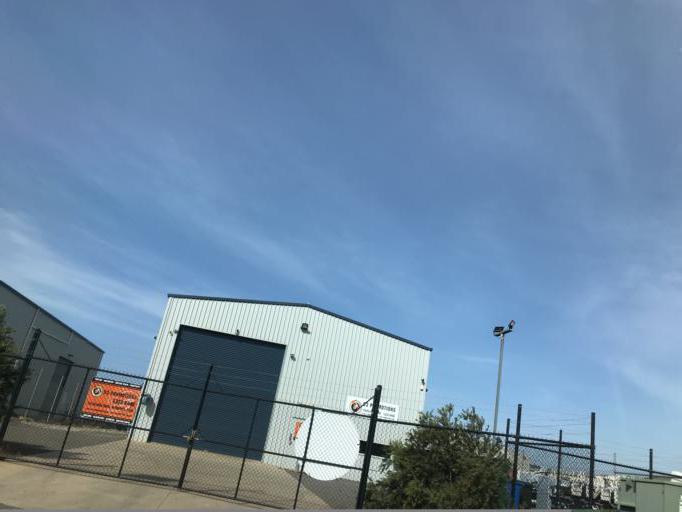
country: AU
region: Victoria
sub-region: Ballarat North
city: Newington
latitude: -37.5358
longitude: 143.8096
